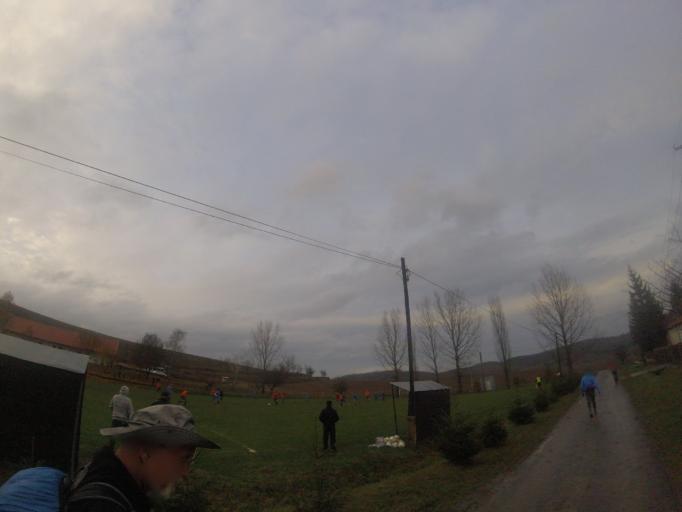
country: HU
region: Nograd
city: Rimoc
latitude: 48.0145
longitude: 19.5084
